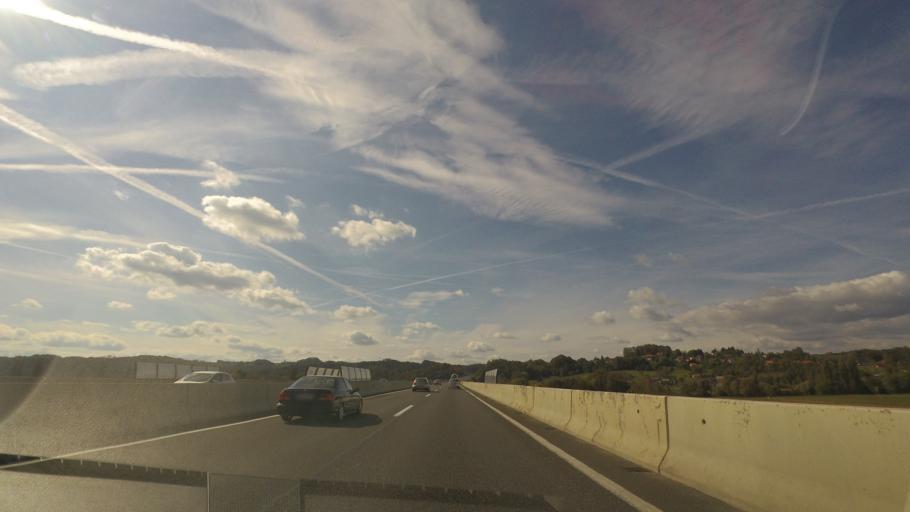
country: HR
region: Karlovacka
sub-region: Grad Karlovac
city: Karlovac
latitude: 45.5112
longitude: 15.5309
